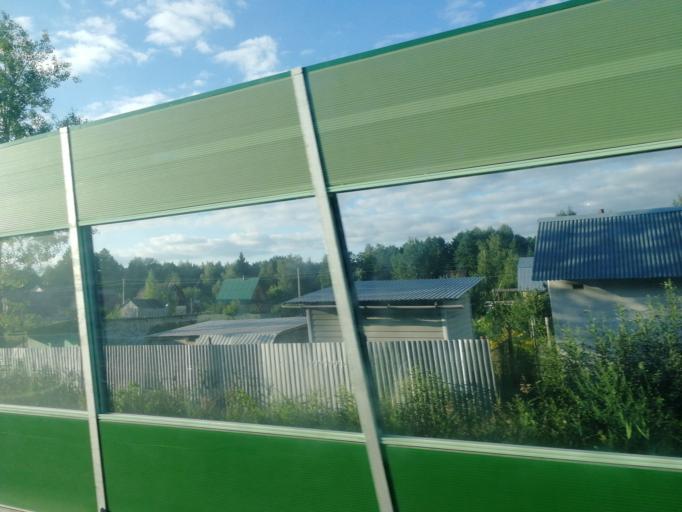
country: RU
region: Kaluga
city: Kaluga
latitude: 54.4547
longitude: 36.2880
